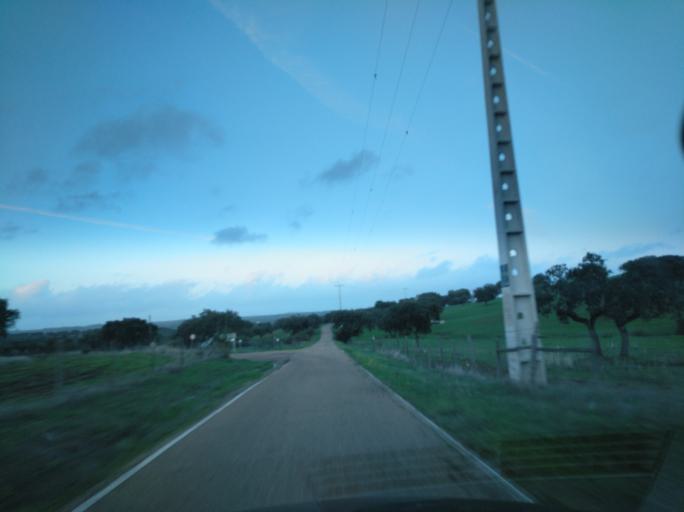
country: PT
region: Portalegre
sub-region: Campo Maior
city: Campo Maior
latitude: 39.0835
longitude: -7.1173
